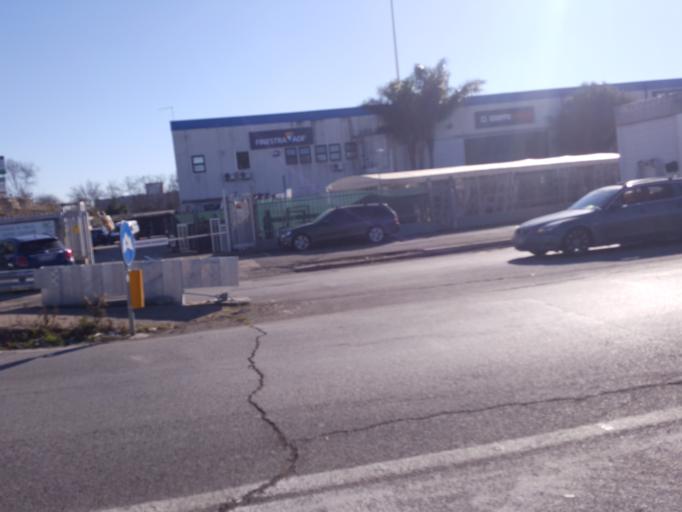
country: IT
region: Latium
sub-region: Citta metropolitana di Roma Capitale
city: Acilia-Castel Fusano-Ostia Antica
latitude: 41.7747
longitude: 12.3341
